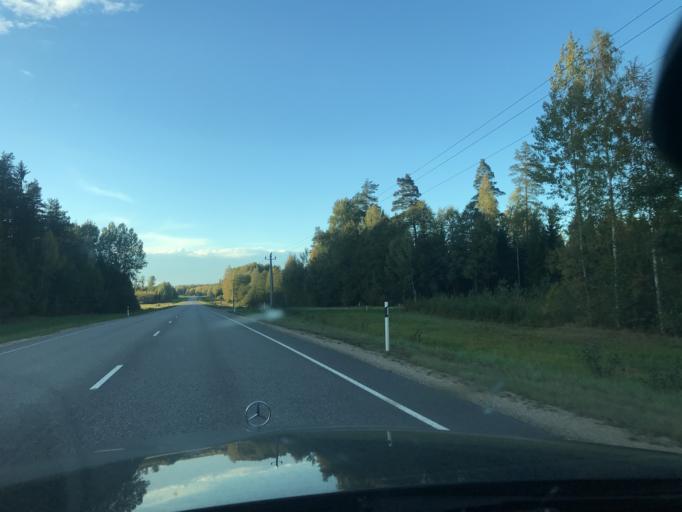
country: EE
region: Vorumaa
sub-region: Voru linn
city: Voru
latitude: 57.8411
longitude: 27.0525
